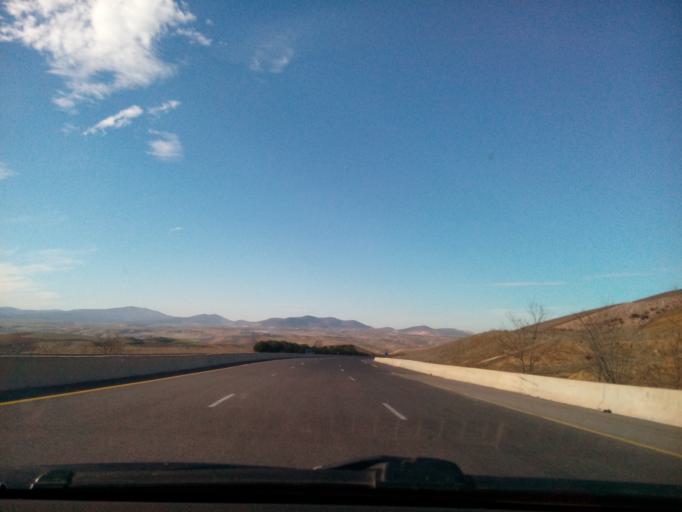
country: DZ
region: Tlemcen
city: Ouled Mimoun
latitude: 35.0288
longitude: -0.9966
